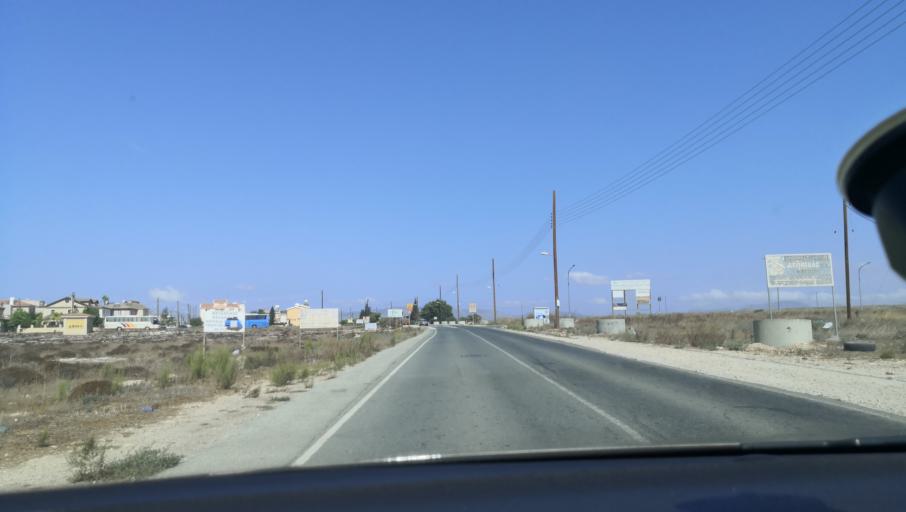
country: CY
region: Lefkosia
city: Mammari
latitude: 35.1647
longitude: 33.2023
